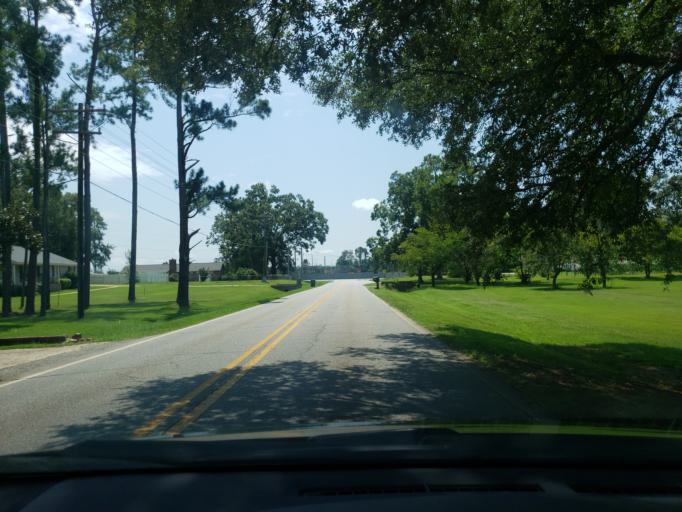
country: US
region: Georgia
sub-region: Dougherty County
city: Albany
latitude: 31.5875
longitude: -84.2810
